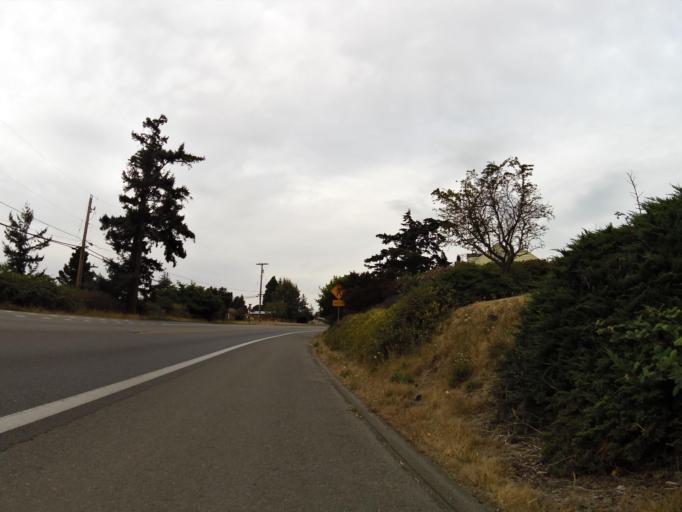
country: US
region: Washington
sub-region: Jefferson County
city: Port Townsend
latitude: 48.1031
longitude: -122.7882
